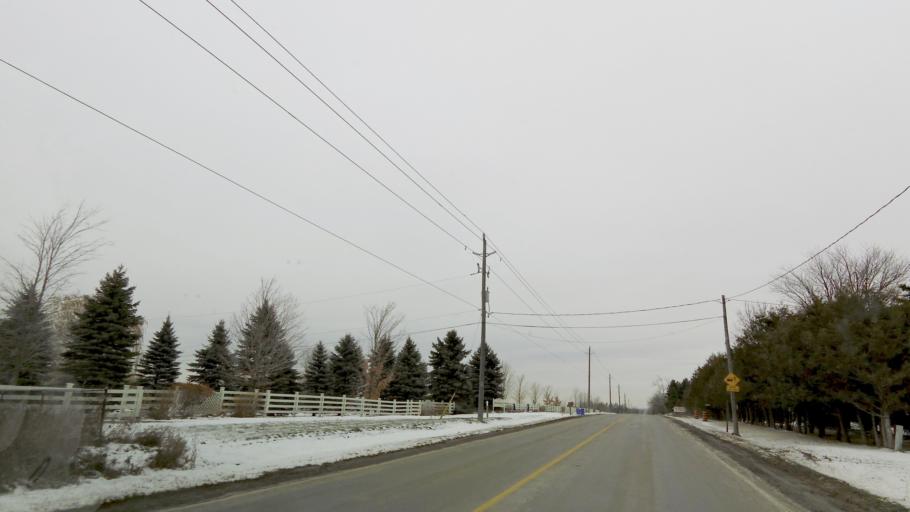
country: CA
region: Ontario
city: Vaughan
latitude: 43.8955
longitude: -79.5942
